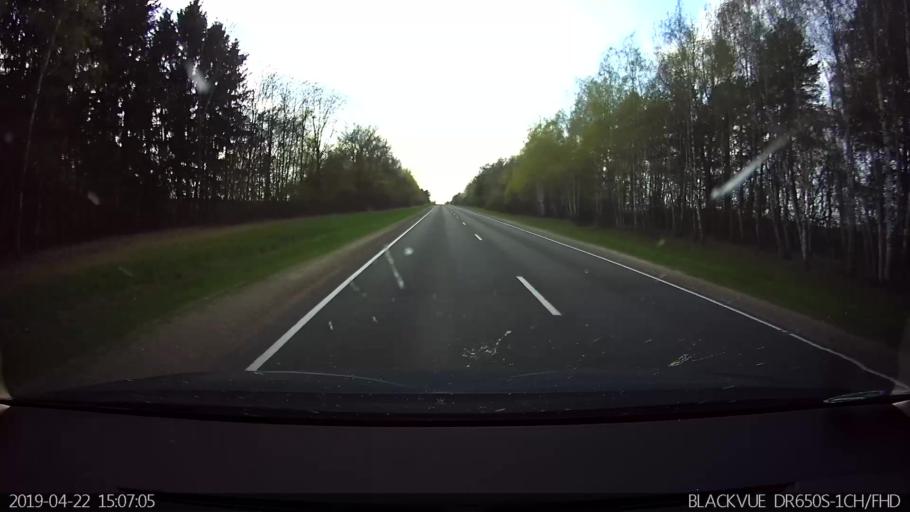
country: BY
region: Brest
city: Kamyanyets
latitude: 52.3297
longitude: 23.8186
